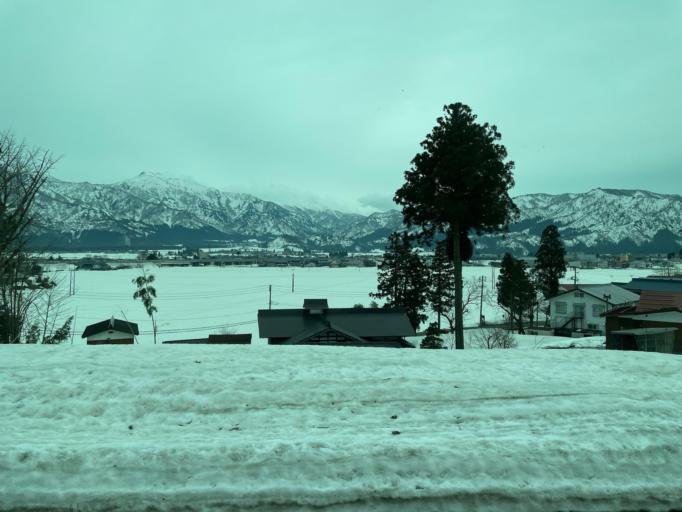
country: JP
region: Niigata
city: Shiozawa
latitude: 37.0310
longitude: 138.8324
